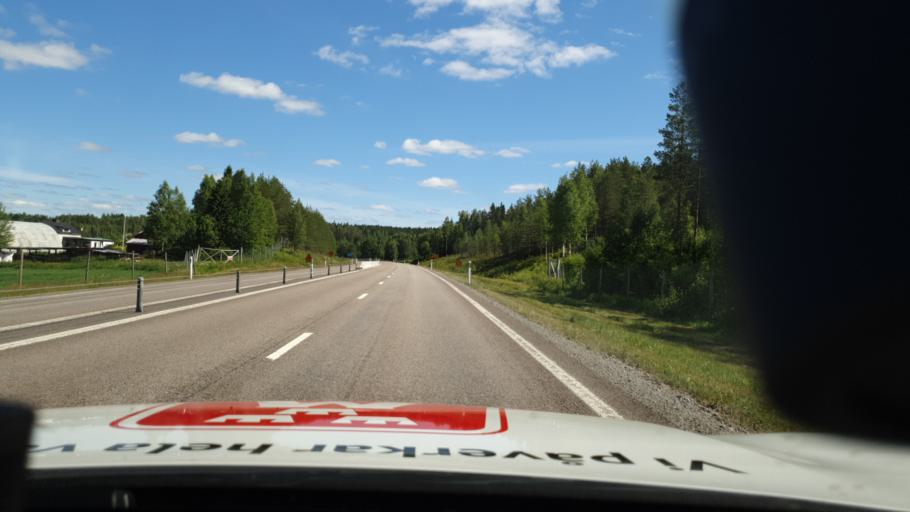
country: SE
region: Norrbotten
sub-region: Kalix Kommun
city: Rolfs
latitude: 65.8819
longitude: 22.9396
